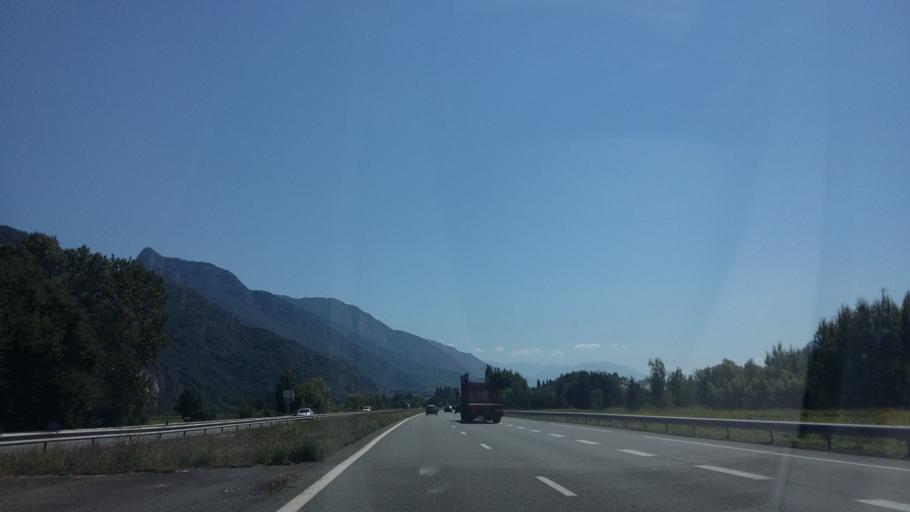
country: FR
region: Rhone-Alpes
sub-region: Departement de l'Isere
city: La Buisse
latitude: 45.3185
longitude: 5.6092
